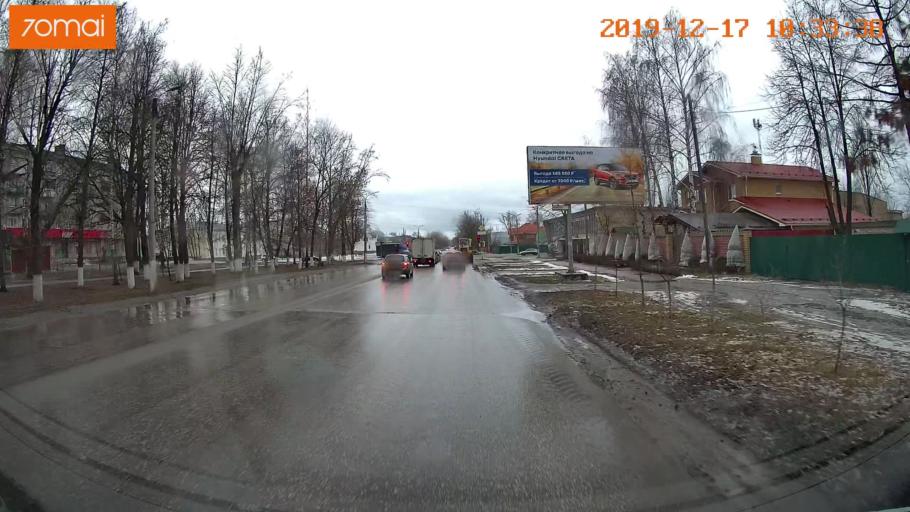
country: RU
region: Vladimir
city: Gus'-Khrustal'nyy
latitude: 55.6217
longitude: 40.6796
